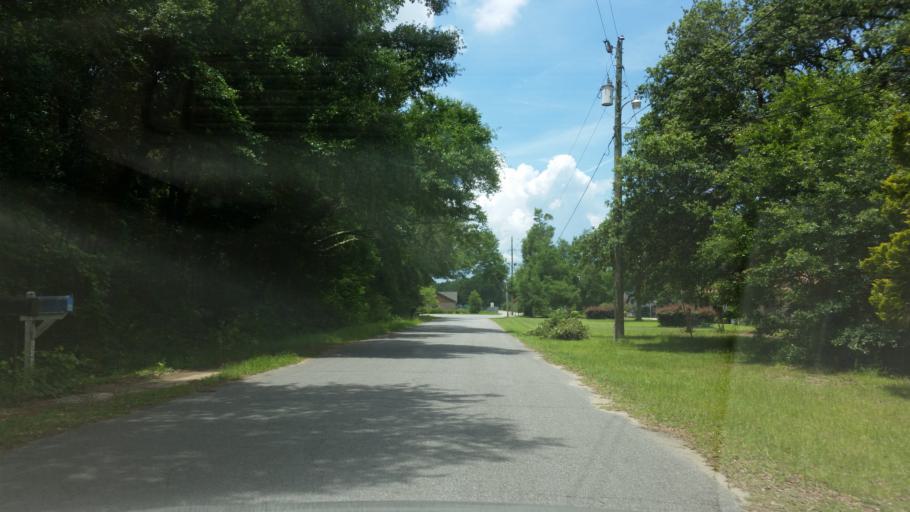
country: US
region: Florida
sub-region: Escambia County
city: Gonzalez
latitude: 30.5468
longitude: -87.3111
